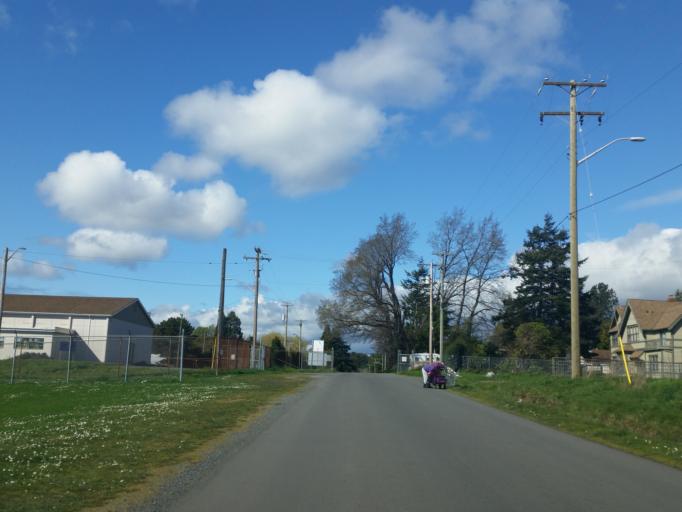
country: CA
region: British Columbia
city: Victoria
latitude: 48.4212
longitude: -123.4064
